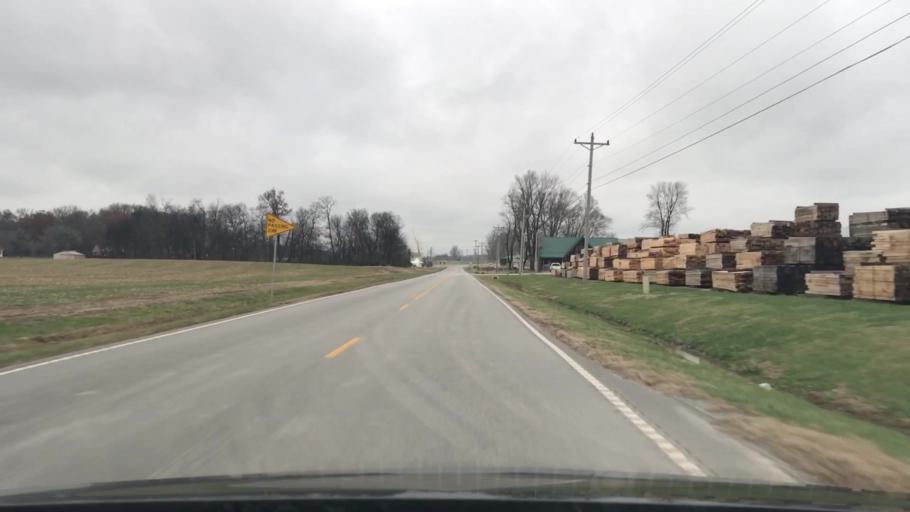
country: US
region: Kentucky
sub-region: Todd County
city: Guthrie
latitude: 36.6990
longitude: -87.1988
